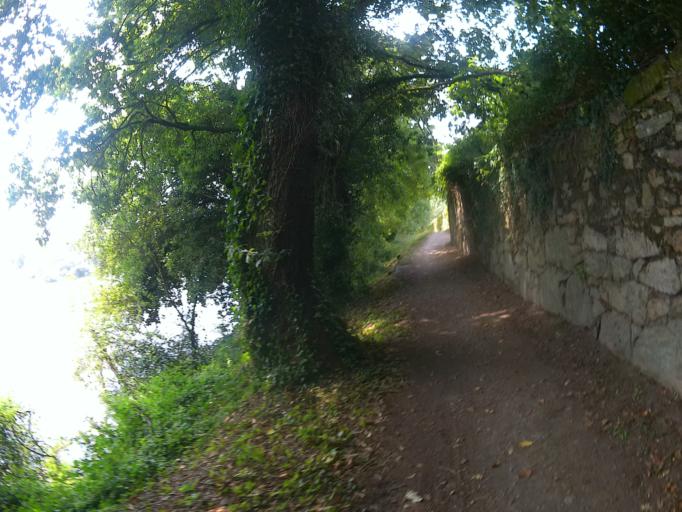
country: PT
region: Viana do Castelo
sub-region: Ponte de Lima
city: Ponte de Lima
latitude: 41.7751
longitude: -8.5851
